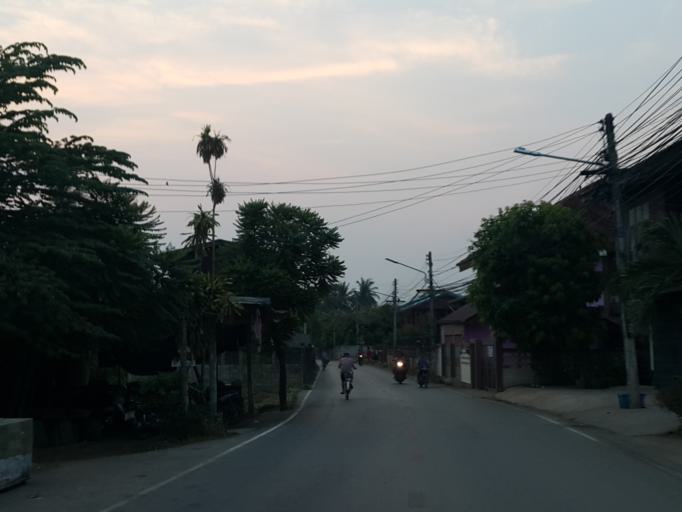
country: TH
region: Sukhothai
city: Sawankhalok
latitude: 17.3134
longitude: 99.8261
